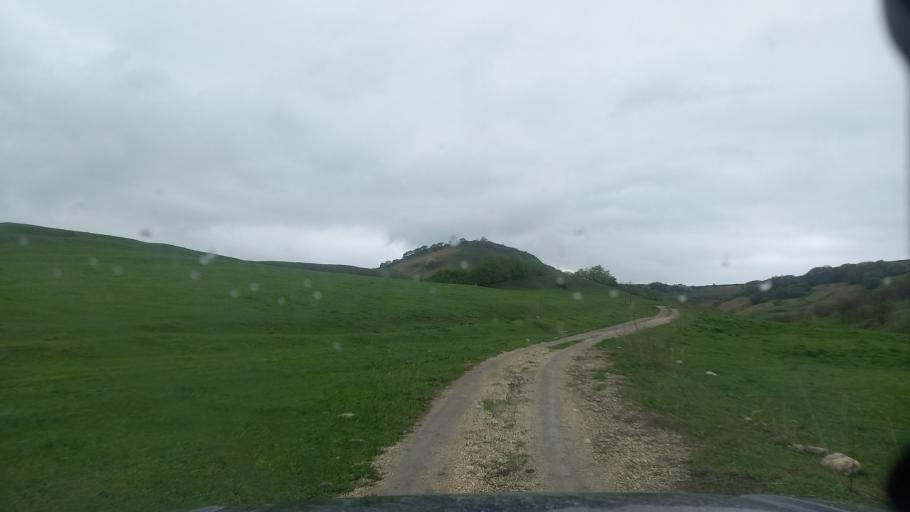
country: RU
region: Kabardino-Balkariya
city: Kamennomostskoye
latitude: 43.7074
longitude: 43.0711
